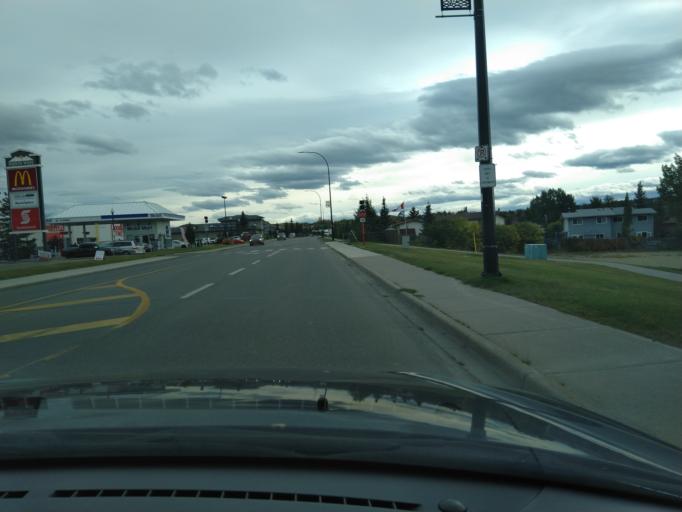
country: CA
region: Alberta
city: Cochrane
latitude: 51.1884
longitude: -114.4756
